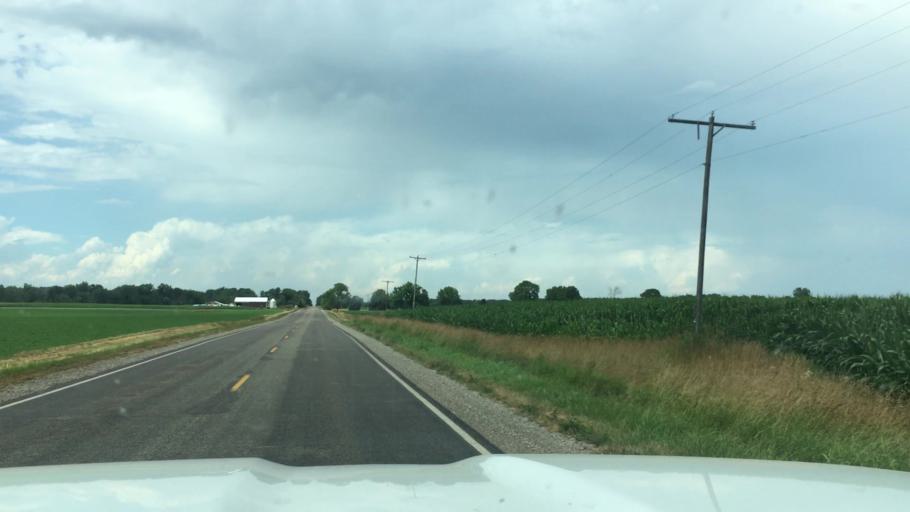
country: US
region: Michigan
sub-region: Montcalm County
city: Carson City
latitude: 43.2259
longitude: -84.7776
